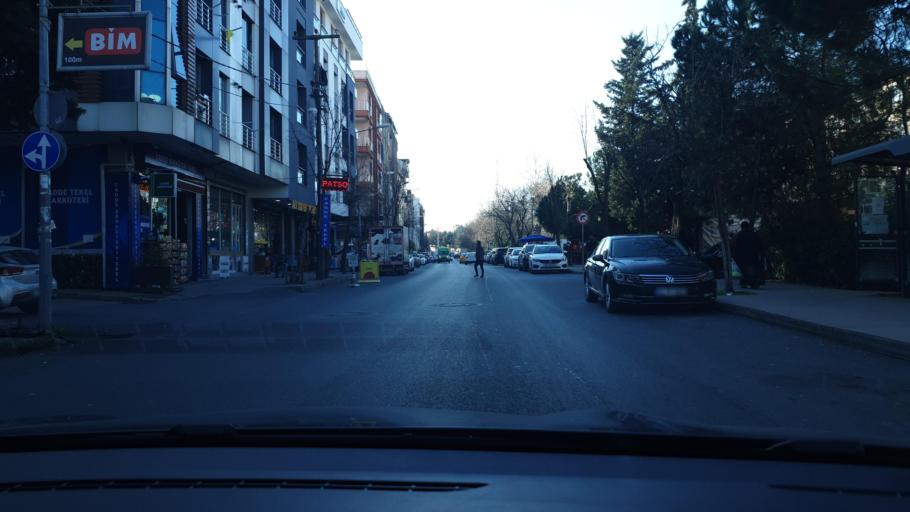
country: TR
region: Istanbul
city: Sisli
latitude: 41.0779
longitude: 28.9611
